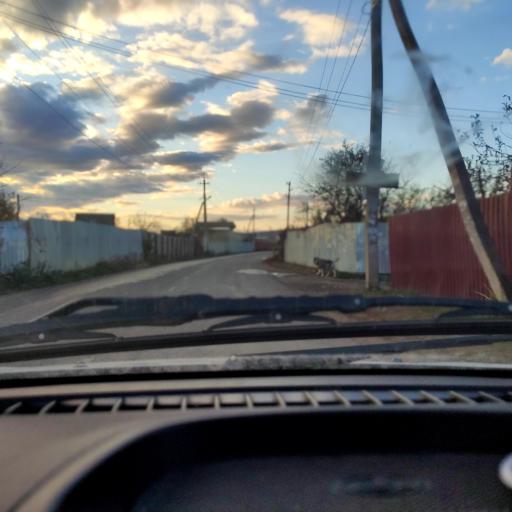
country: RU
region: Samara
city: Povolzhskiy
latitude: 53.4656
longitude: 49.6575
